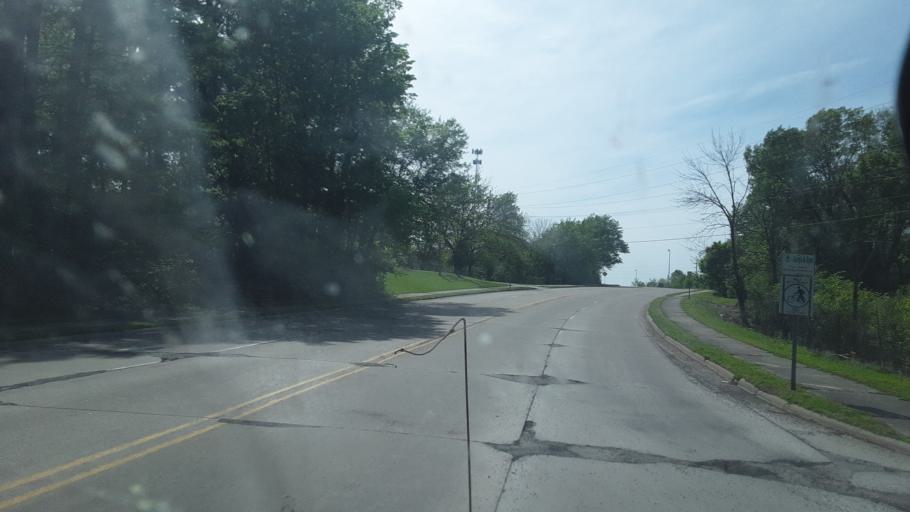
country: US
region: Illinois
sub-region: Jackson County
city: Carbondale
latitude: 37.7001
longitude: -89.2093
